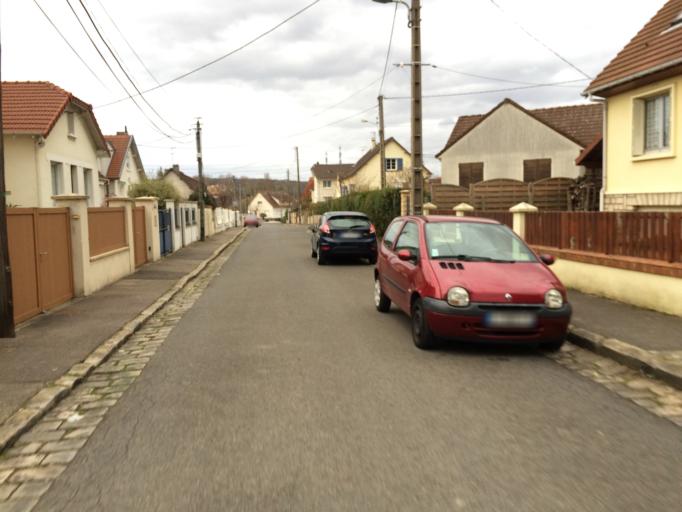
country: FR
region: Ile-de-France
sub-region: Departement de l'Essonne
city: Igny
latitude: 48.7342
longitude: 2.2193
